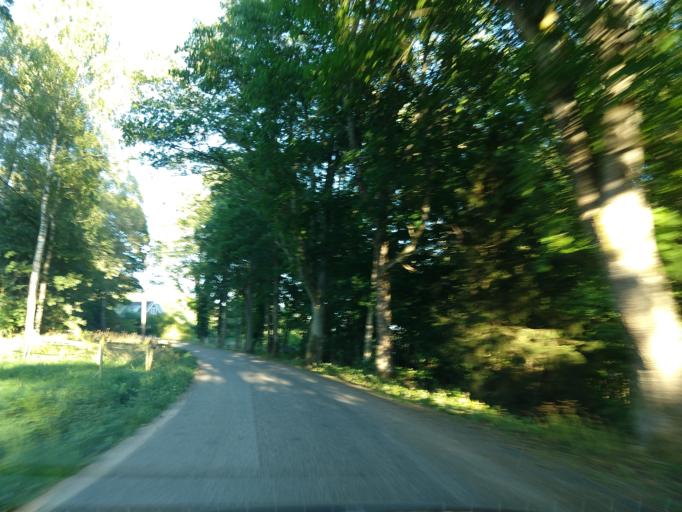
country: SE
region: Blekinge
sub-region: Ronneby Kommun
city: Brakne-Hoby
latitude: 56.2596
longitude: 15.1331
